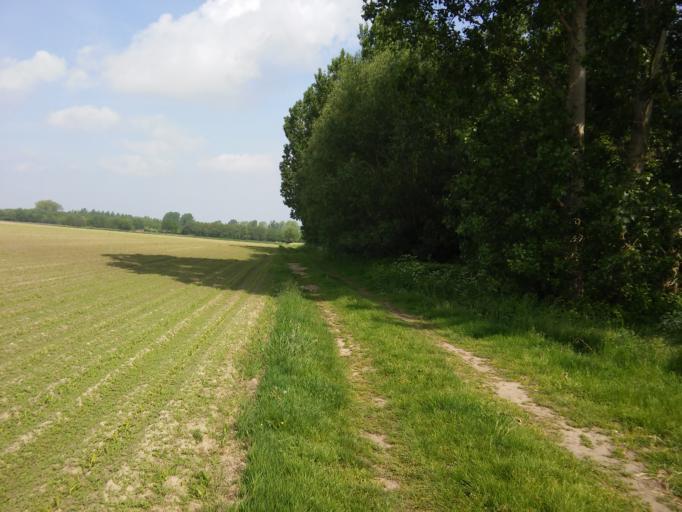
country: BE
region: Flanders
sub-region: Provincie Antwerpen
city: Mechelen
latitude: 51.0226
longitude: 4.4381
